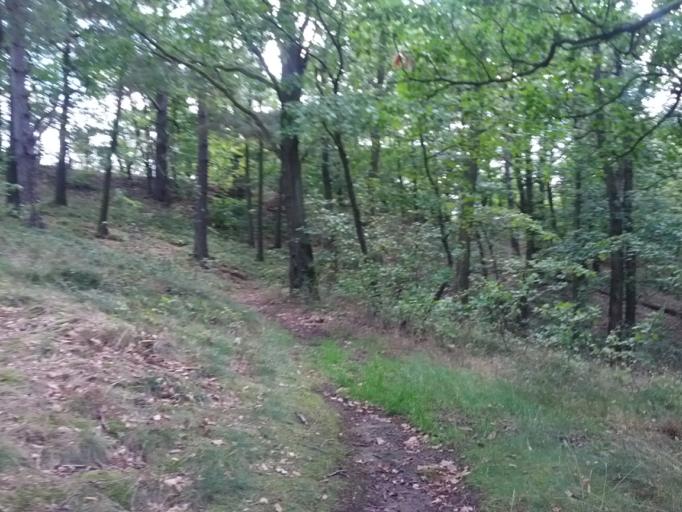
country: DE
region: Thuringia
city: Eisenach
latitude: 50.9605
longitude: 10.3179
